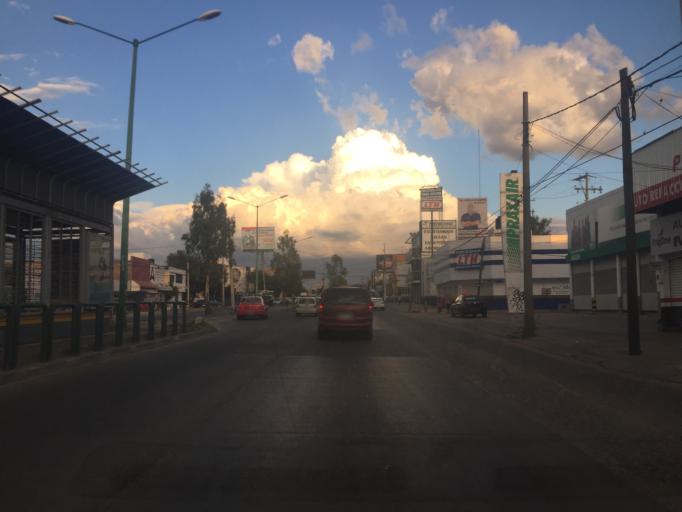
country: MX
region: Guanajuato
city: Leon
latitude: 21.0978
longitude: -101.6424
